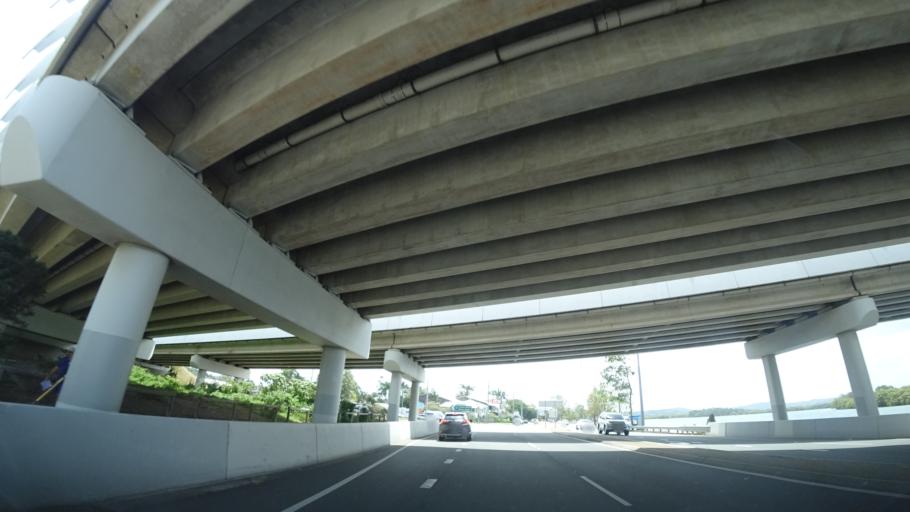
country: AU
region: Queensland
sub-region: Sunshine Coast
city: Buderim
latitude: -26.6425
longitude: 153.0673
